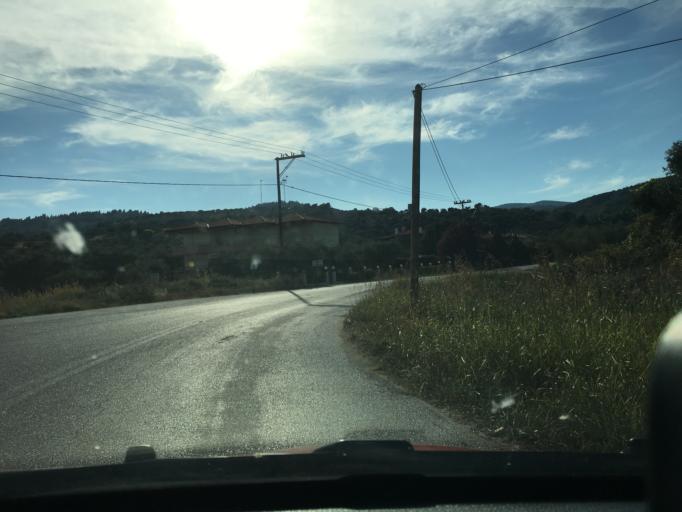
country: GR
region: Central Macedonia
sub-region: Nomos Chalkidikis
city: Agios Nikolaos
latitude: 40.2937
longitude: 23.6937
